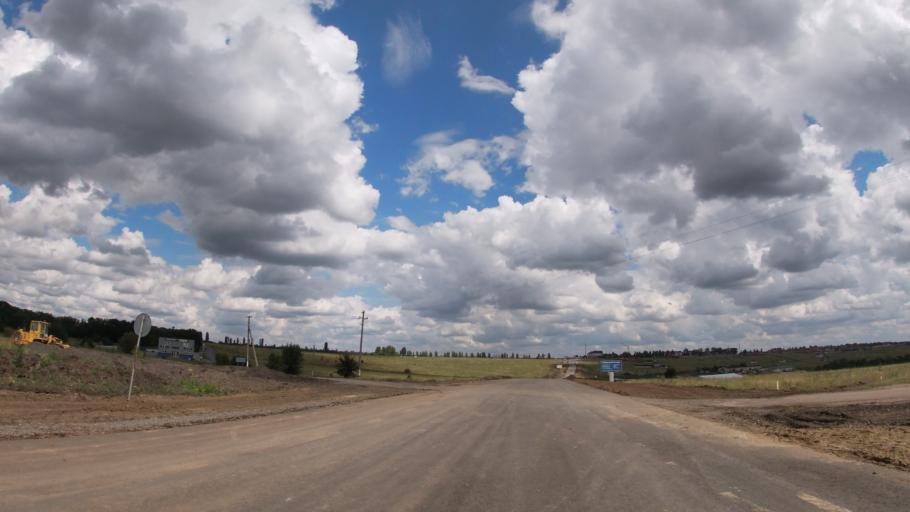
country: RU
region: Belgorod
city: Mayskiy
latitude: 50.5224
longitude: 36.5082
